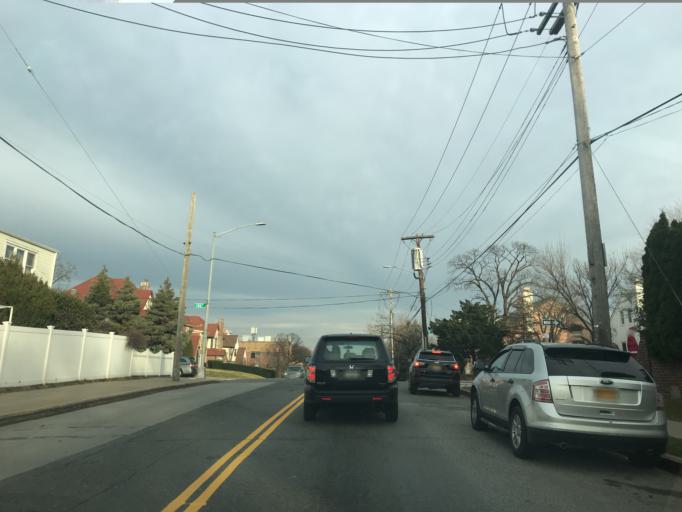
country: US
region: New York
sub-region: Nassau County
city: East Atlantic Beach
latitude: 40.7871
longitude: -73.8211
